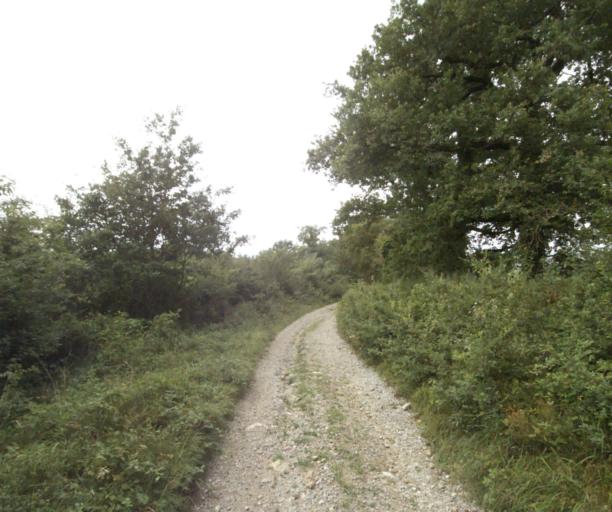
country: FR
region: Midi-Pyrenees
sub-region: Departement du Tarn
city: Soreze
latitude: 43.4575
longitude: 2.0896
